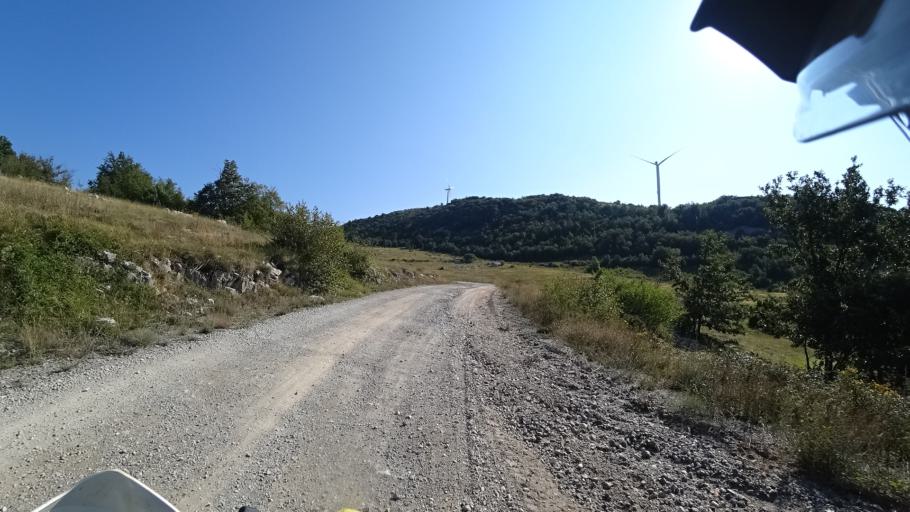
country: HR
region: Zadarska
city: Gracac
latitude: 44.2573
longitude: 16.0732
